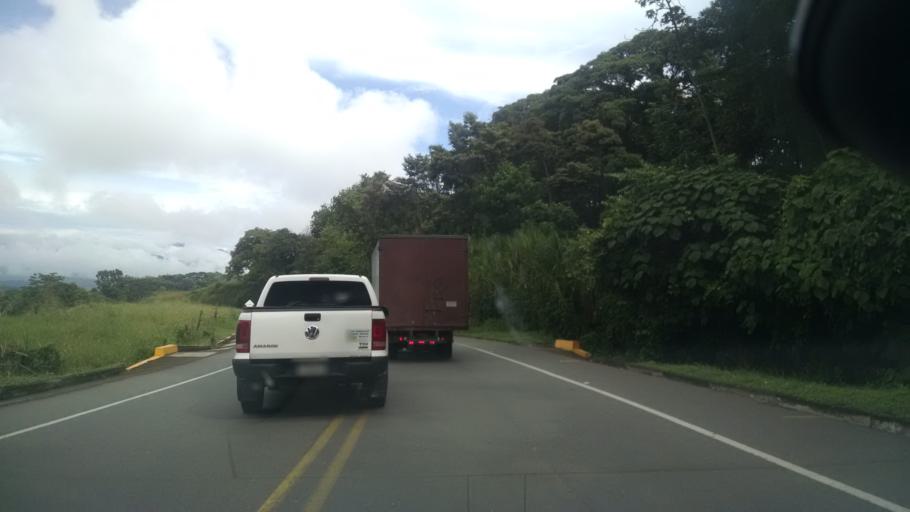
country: CO
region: Caldas
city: Palestina
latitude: 5.0933
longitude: -75.6502
